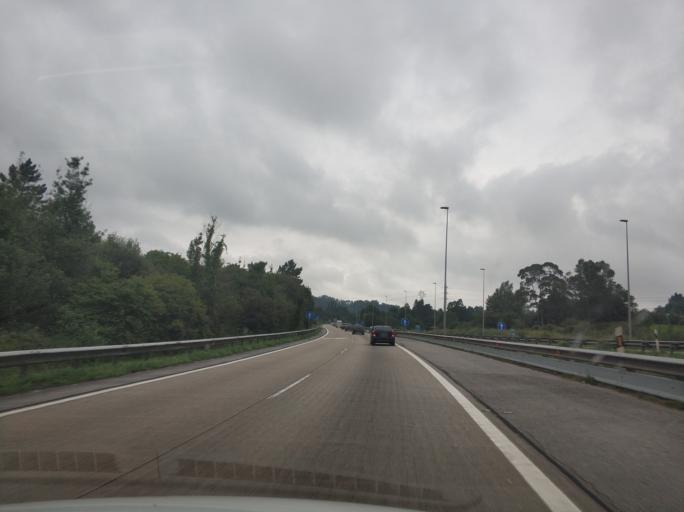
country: ES
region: Asturias
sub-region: Province of Asturias
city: Corvera de Asturias
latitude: 43.5027
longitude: -5.7922
